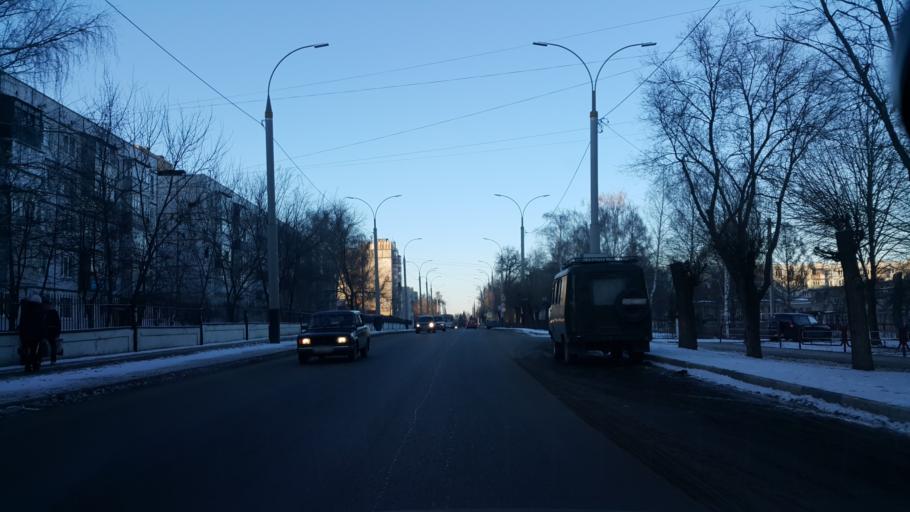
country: RU
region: Tambov
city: Pokrovo-Prigorodnoye
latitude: 52.7056
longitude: 41.3989
